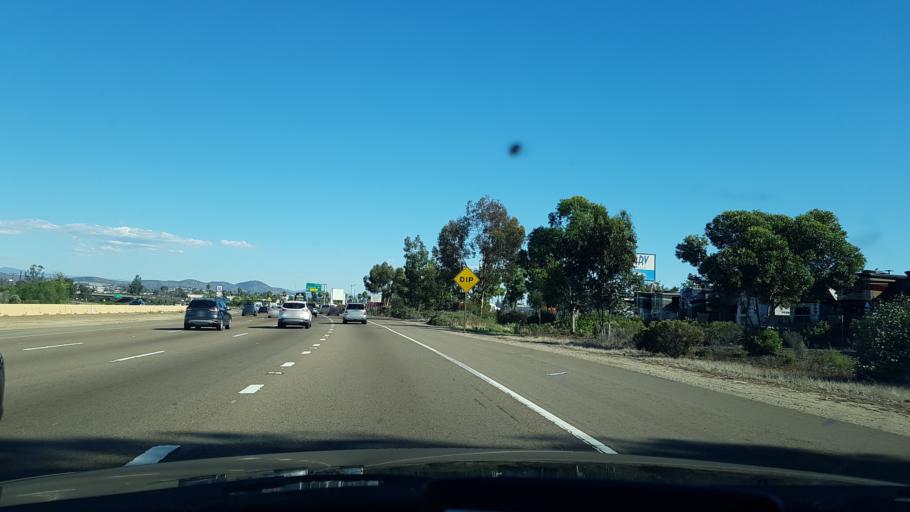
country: US
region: California
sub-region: San Diego County
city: La Jolla
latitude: 32.8380
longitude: -117.1591
